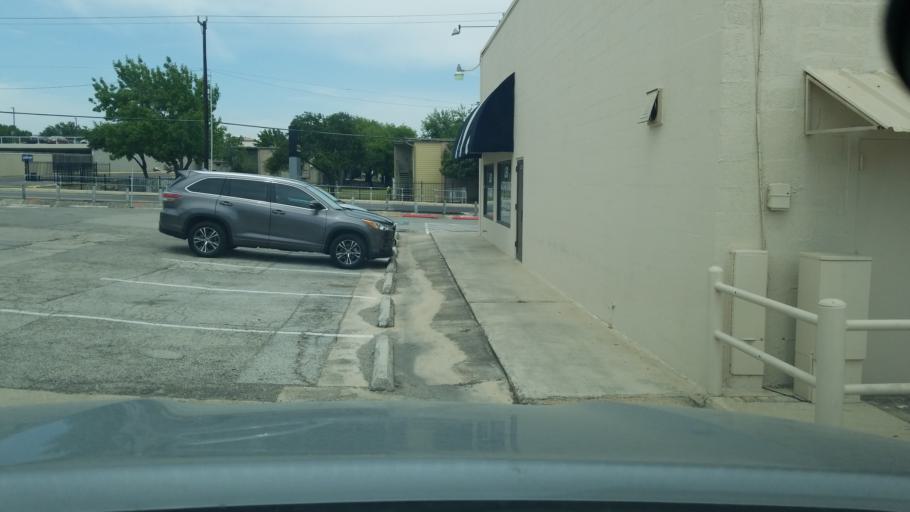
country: US
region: Texas
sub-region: Bexar County
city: Castle Hills
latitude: 29.5298
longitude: -98.4954
